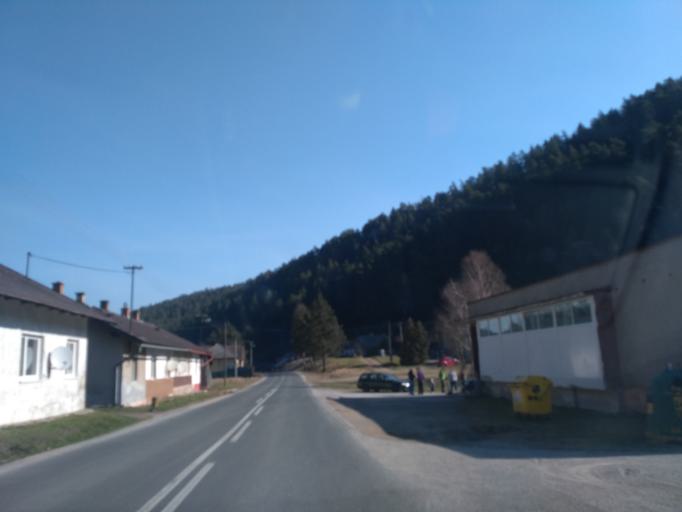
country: SK
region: Kosicky
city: Medzev
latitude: 48.7475
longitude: 20.7755
